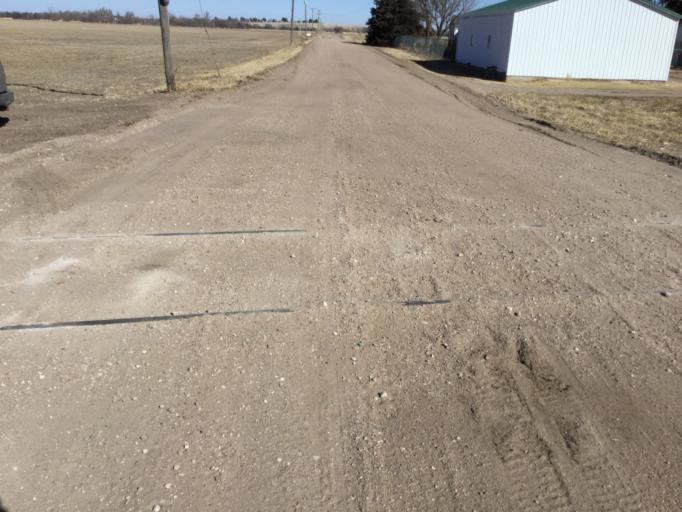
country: US
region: Kansas
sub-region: Pawnee County
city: Larned
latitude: 38.1660
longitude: -99.1318
